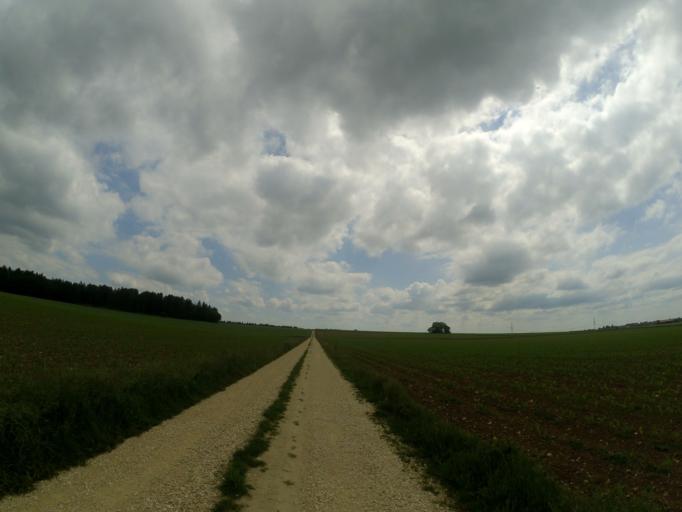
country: DE
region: Baden-Wuerttemberg
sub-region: Tuebingen Region
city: Blaubeuren
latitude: 48.4250
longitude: 9.8295
